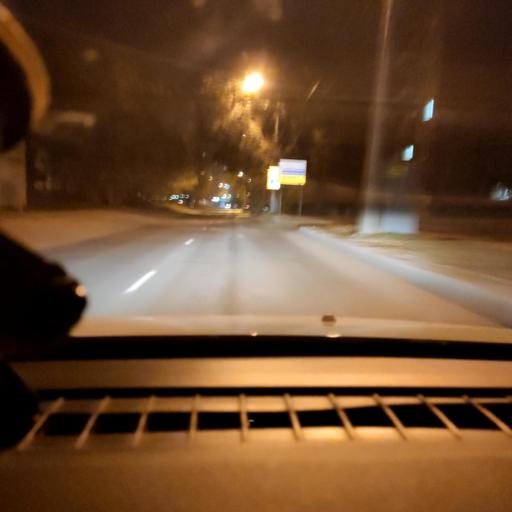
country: RU
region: Samara
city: Rozhdestveno
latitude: 53.1433
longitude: 50.0458
